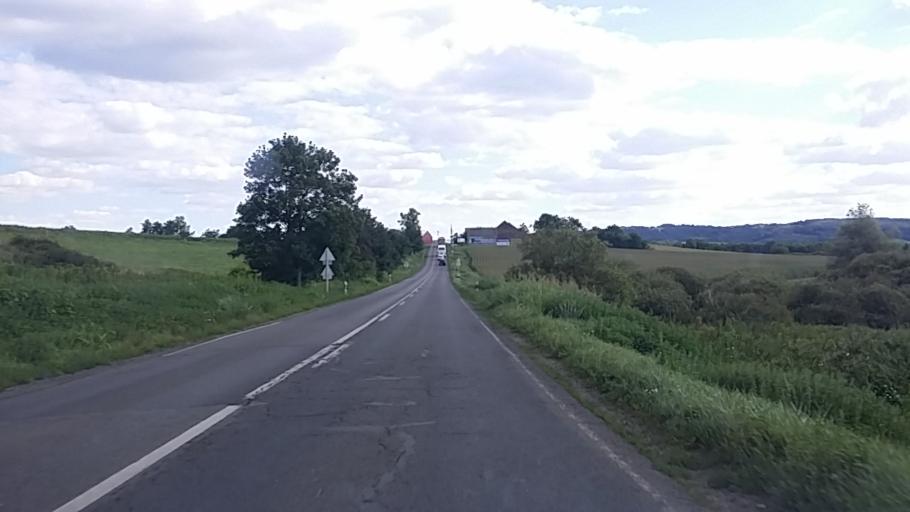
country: HU
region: Baranya
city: Sasd
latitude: 46.2288
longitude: 18.1216
